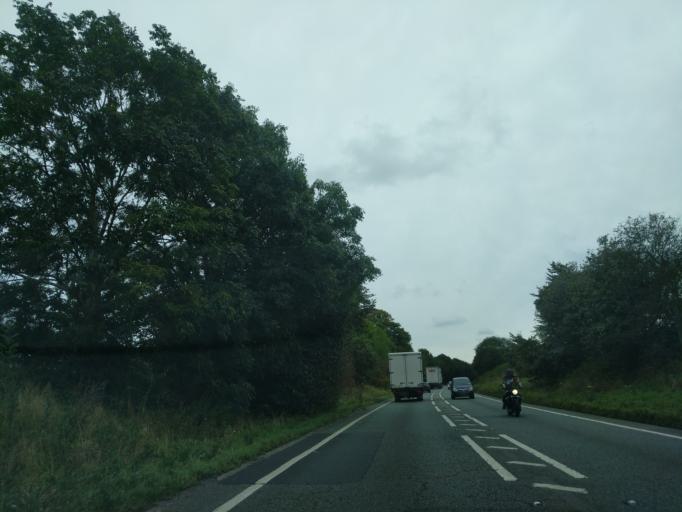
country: GB
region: England
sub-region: Cheshire East
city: Weston
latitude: 53.0729
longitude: -2.3517
